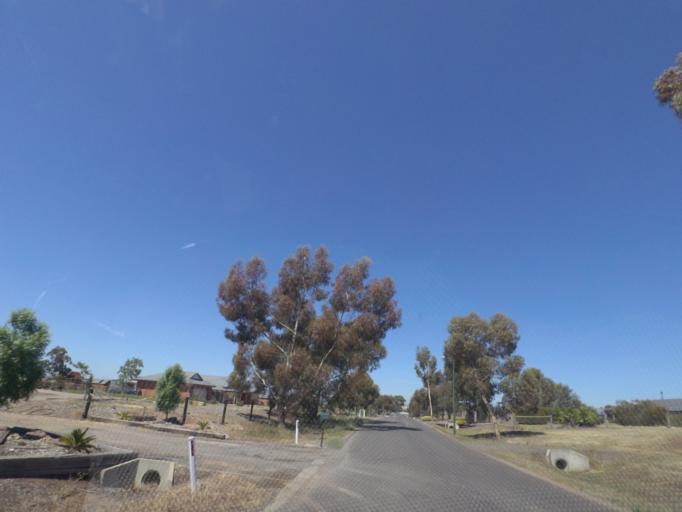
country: AU
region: Victoria
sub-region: Melton
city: Brookfield
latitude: -37.7024
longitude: 144.5057
